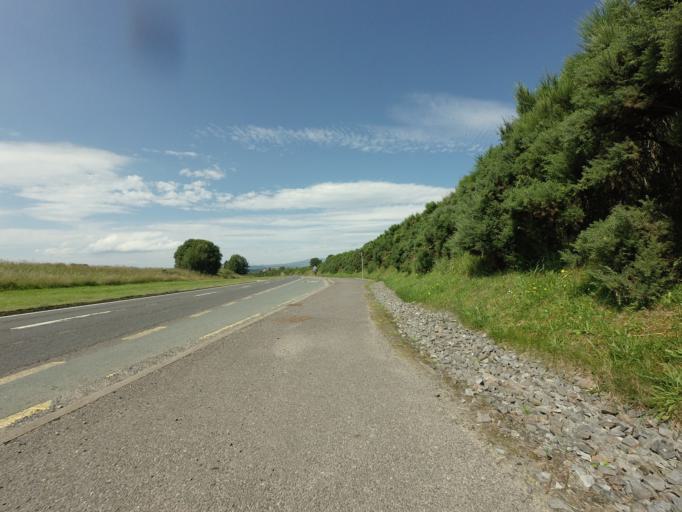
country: GB
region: Scotland
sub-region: Highland
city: Conon Bridge
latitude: 57.5490
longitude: -4.3928
